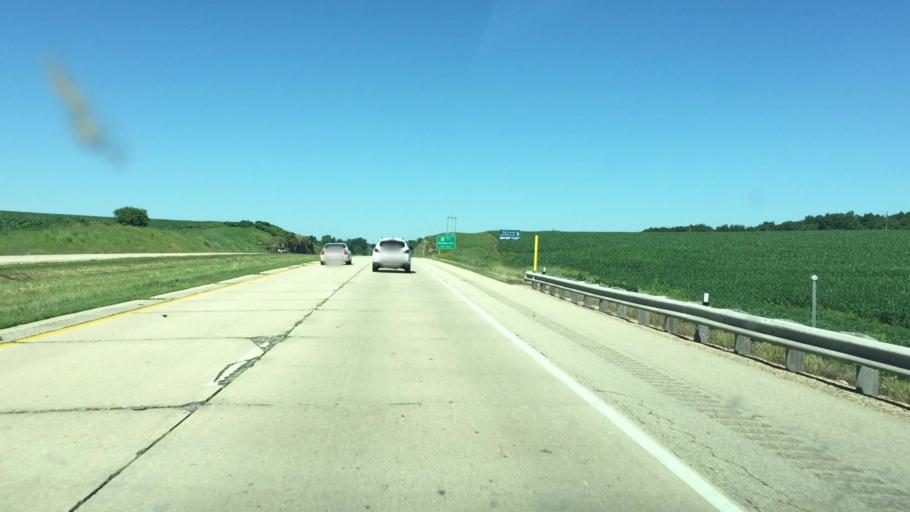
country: US
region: Wisconsin
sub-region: Iowa County
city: Dodgeville
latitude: 42.9463
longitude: -90.1171
